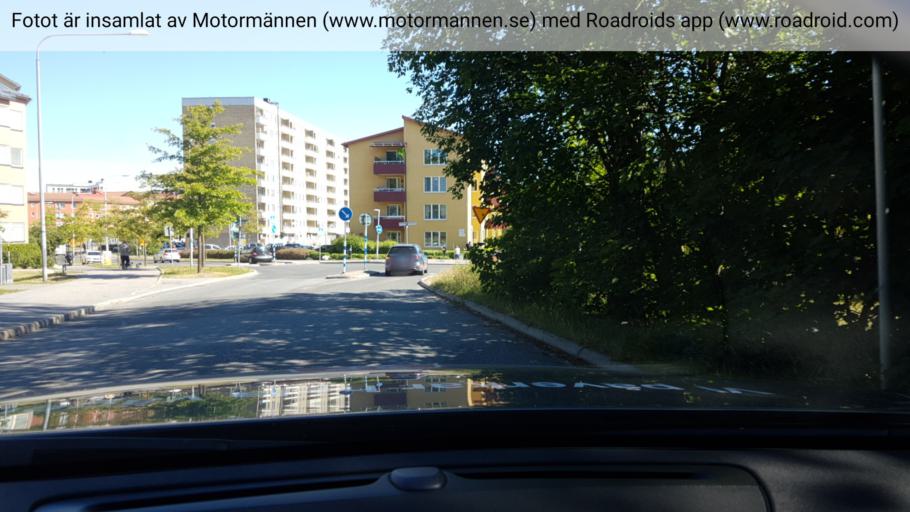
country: SE
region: Stockholm
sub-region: Huddinge Kommun
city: Huddinge
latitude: 59.2388
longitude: 17.9948
